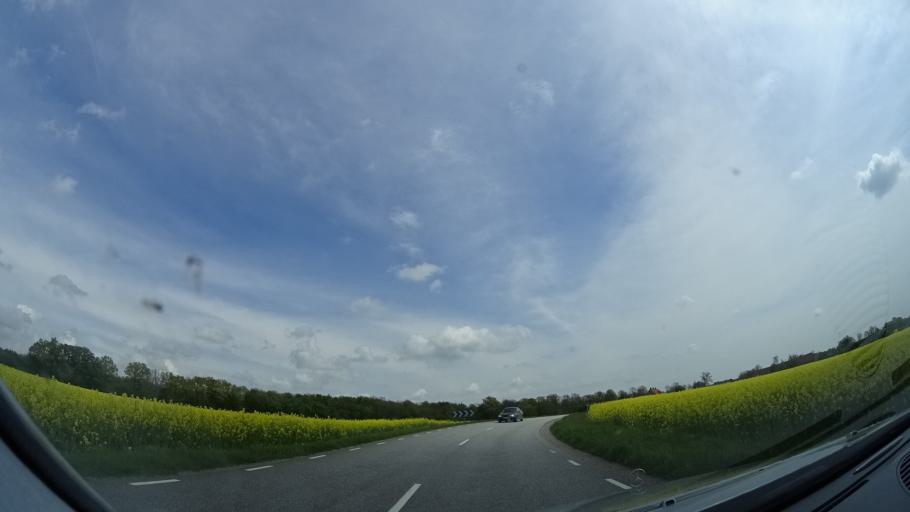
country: SE
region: Skane
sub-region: Sjobo Kommun
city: Blentarp
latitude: 55.7002
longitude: 13.5895
